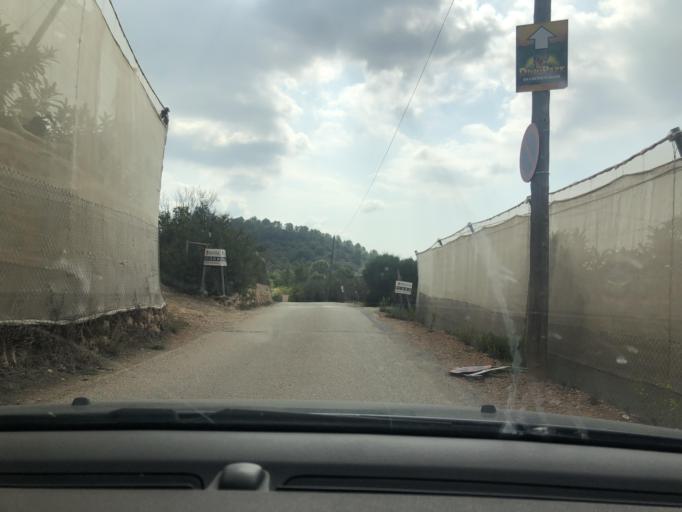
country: ES
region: Valencia
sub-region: Provincia de Alicante
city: Callosa d'En Sarria
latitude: 38.6561
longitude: -0.0942
